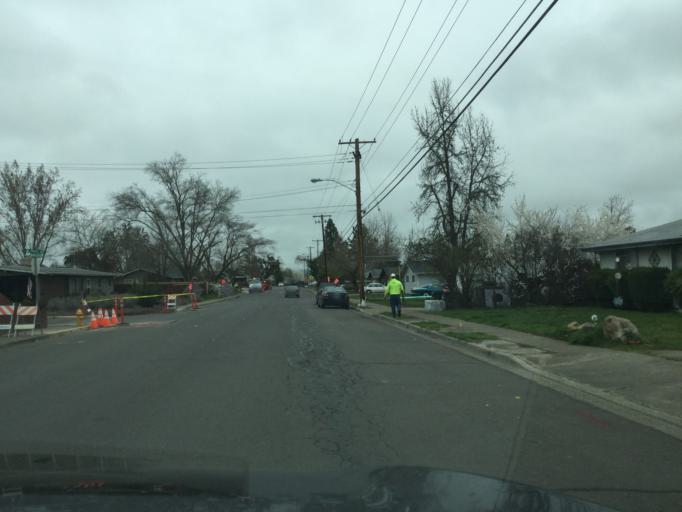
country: US
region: Oregon
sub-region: Jackson County
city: Central Point
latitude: 42.3838
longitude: -122.9197
